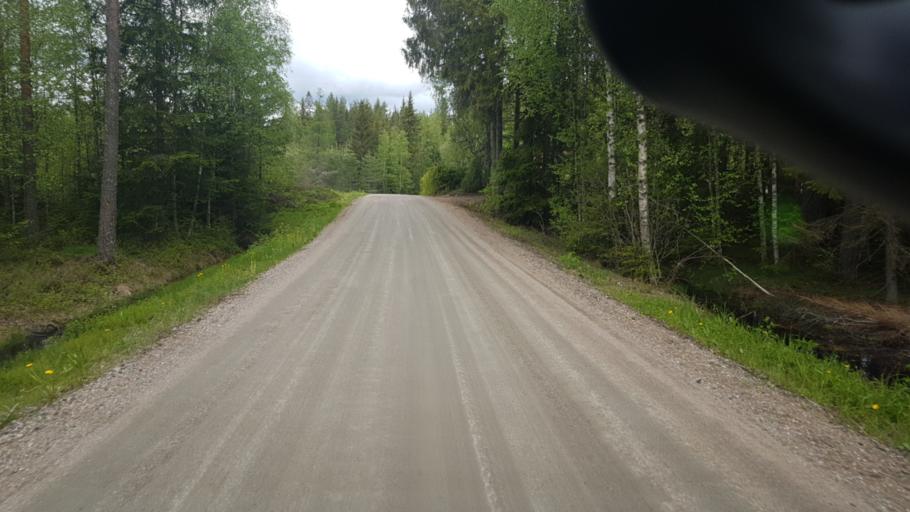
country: SE
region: Vaermland
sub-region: Arvika Kommun
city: Arvika
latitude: 59.8375
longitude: 12.6046
